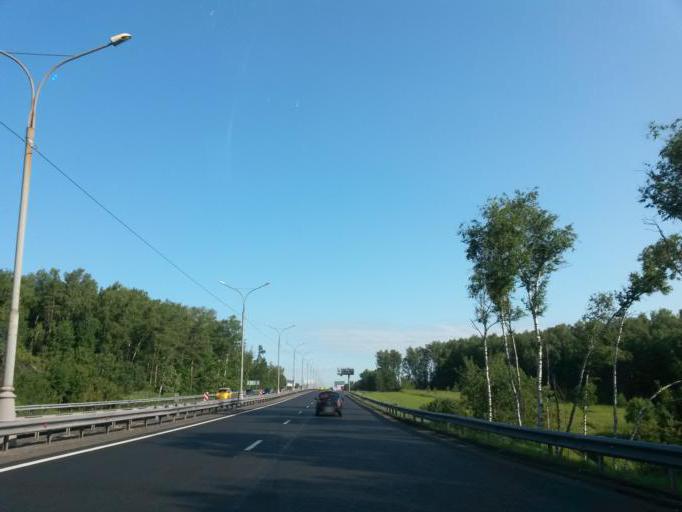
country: RU
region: Moskovskaya
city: Gorki-Leninskiye
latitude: 55.5157
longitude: 37.8274
